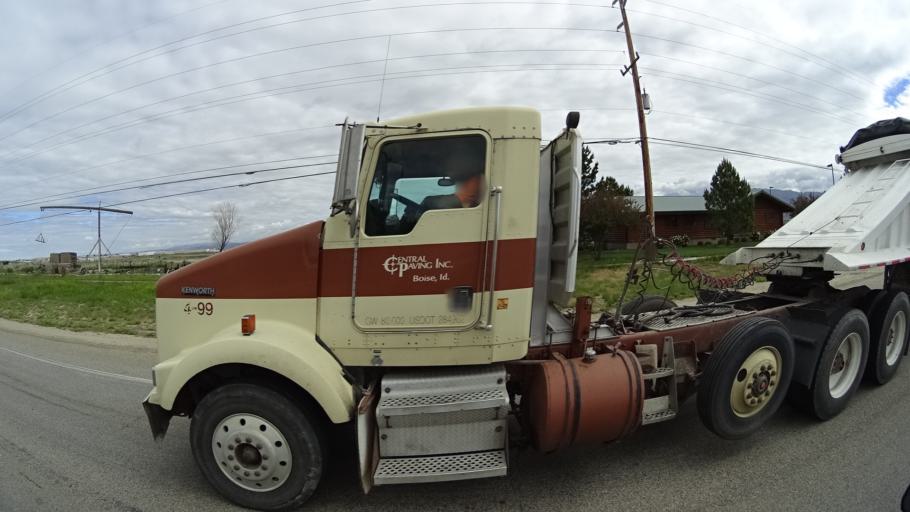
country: US
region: Idaho
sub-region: Ada County
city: Boise
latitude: 43.5456
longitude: -116.1815
